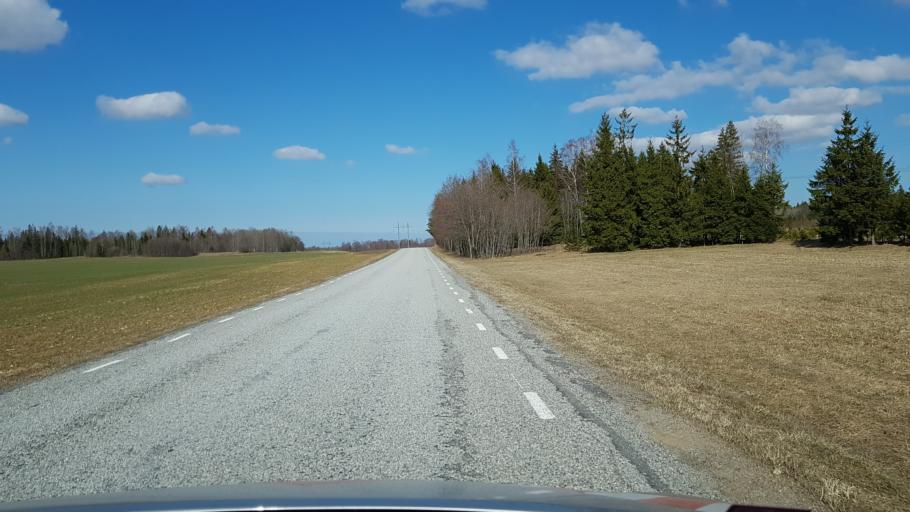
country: EE
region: Laeaene-Virumaa
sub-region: Kadrina vald
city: Kadrina
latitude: 59.2979
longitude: 26.2151
